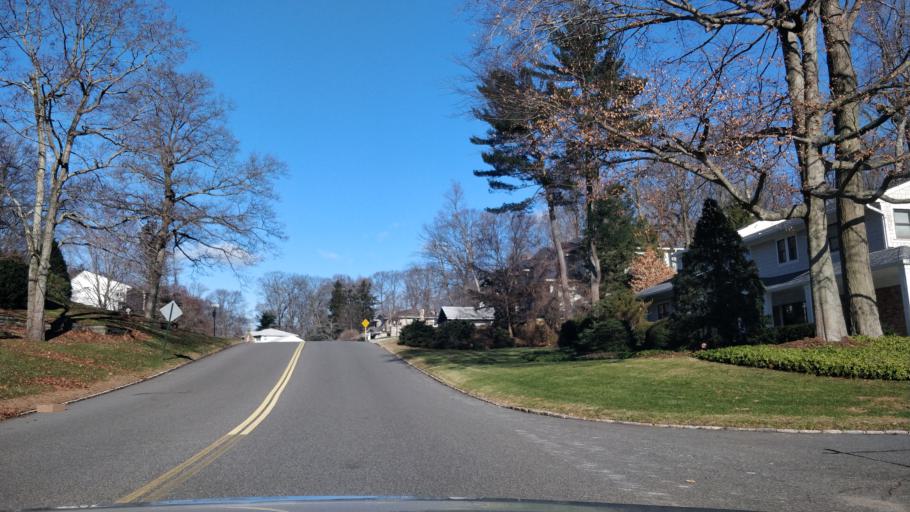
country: US
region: New York
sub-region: Nassau County
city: East Hills
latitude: 40.7967
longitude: -73.6323
